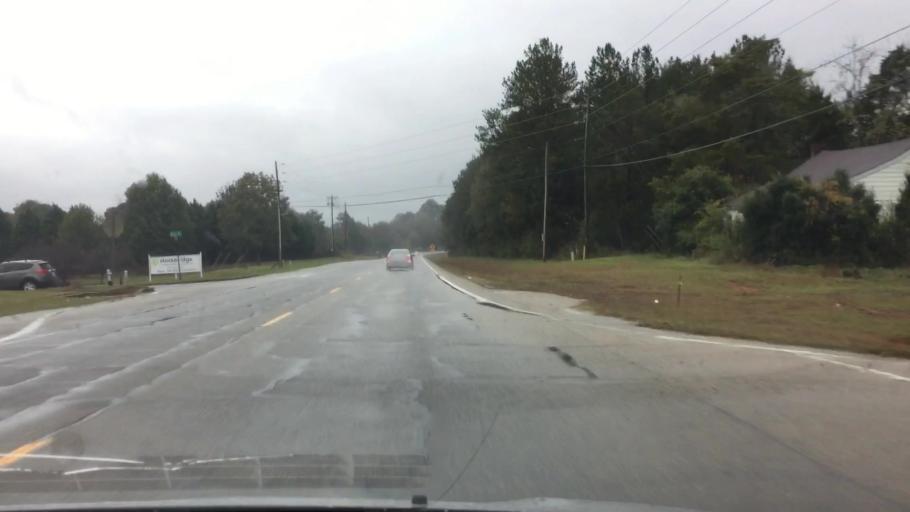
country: US
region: Georgia
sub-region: Henry County
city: Stockbridge
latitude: 33.5675
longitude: -84.1429
